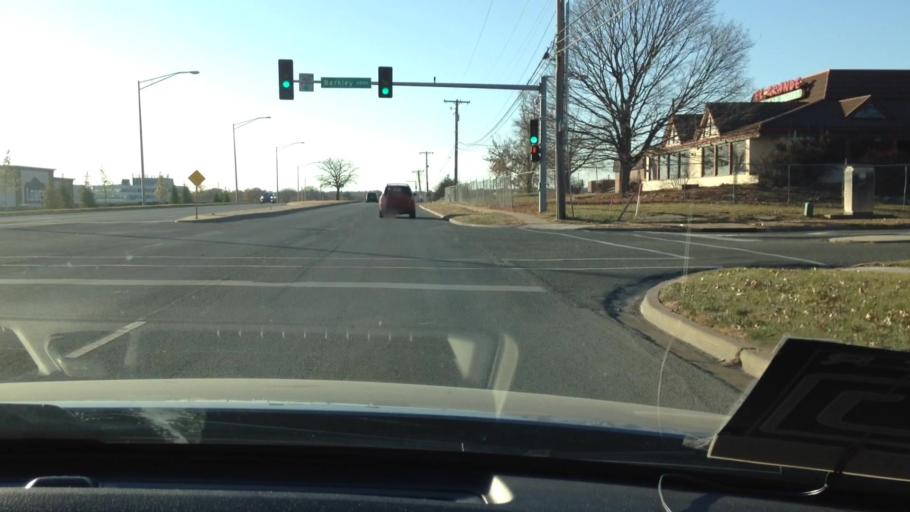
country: US
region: Kansas
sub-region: Johnson County
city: Overland Park
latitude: 38.9568
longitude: -94.6637
